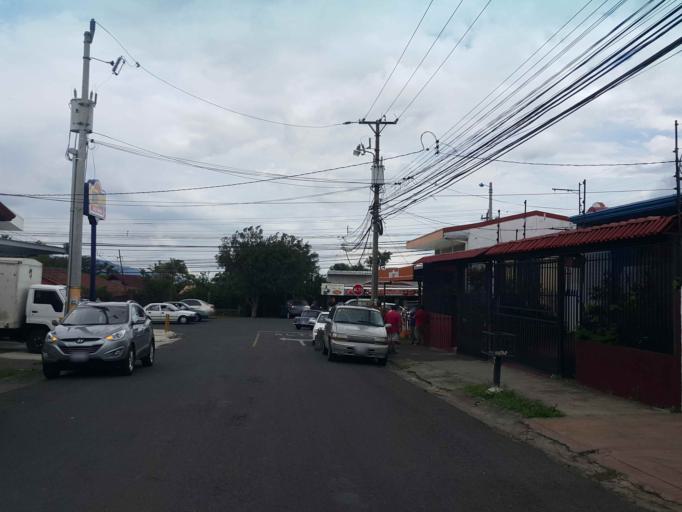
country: CR
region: Heredia
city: Heredia
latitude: 10.0135
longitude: -84.1201
